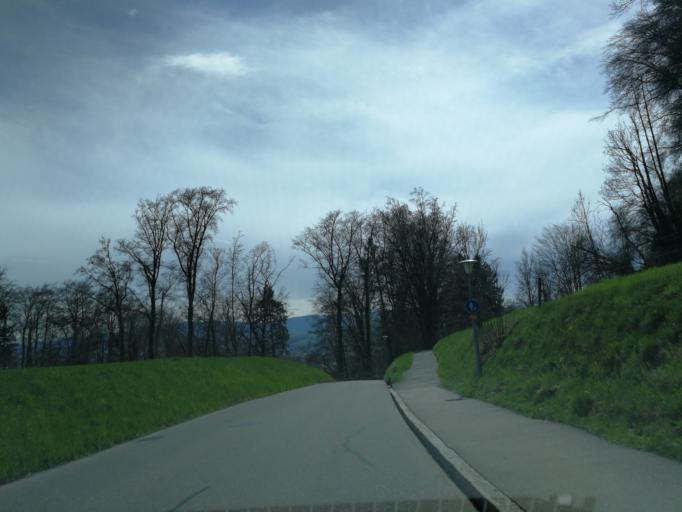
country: CH
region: Zurich
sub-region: Bezirk Meilen
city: Obermeilen
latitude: 47.2730
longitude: 8.6620
